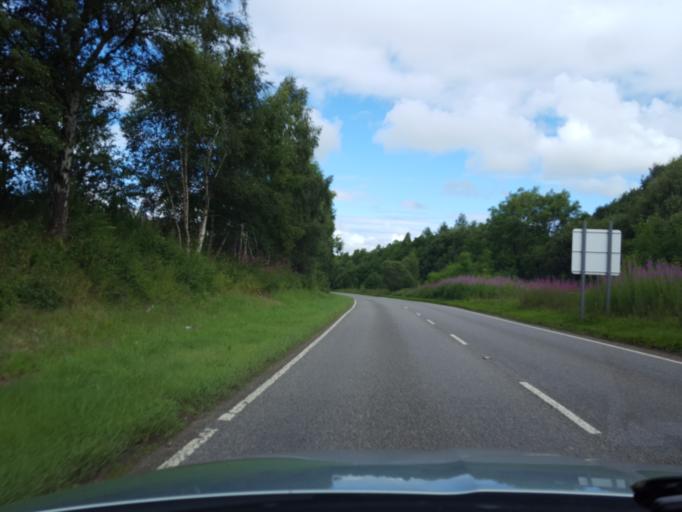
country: GB
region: Scotland
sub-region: Moray
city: Rothes
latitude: 57.5018
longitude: -3.1930
